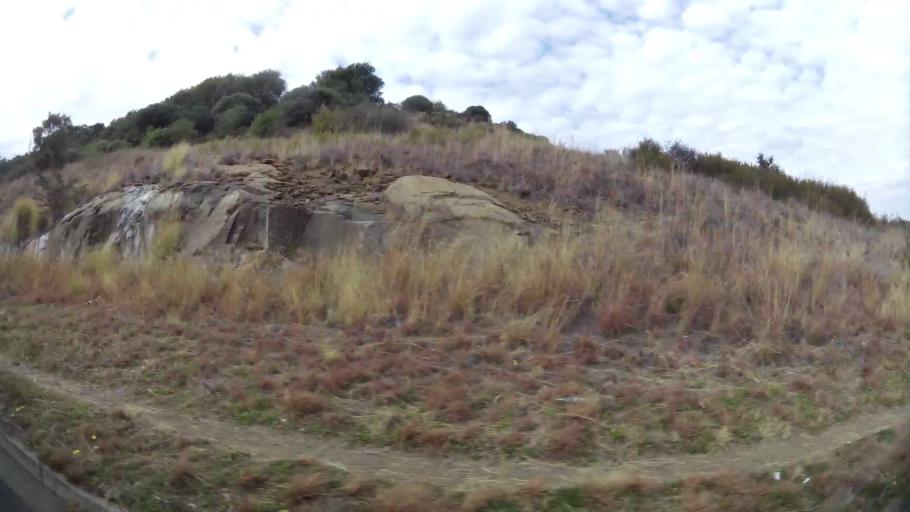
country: ZA
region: Orange Free State
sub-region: Mangaung Metropolitan Municipality
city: Bloemfontein
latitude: -29.1012
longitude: 26.2122
